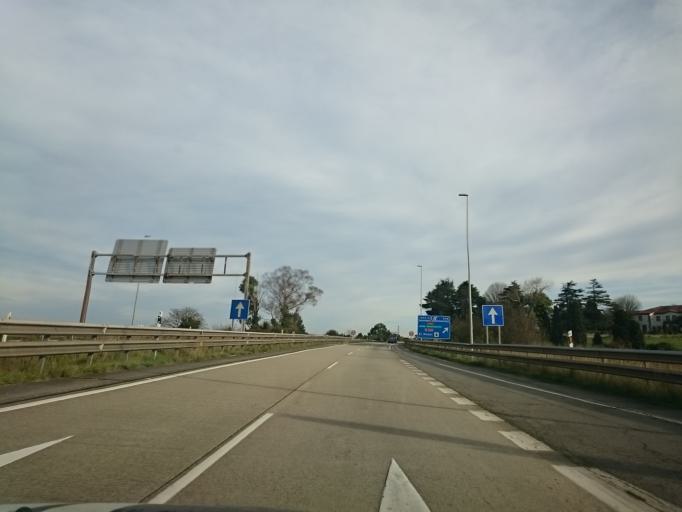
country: ES
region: Asturias
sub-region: Province of Asturias
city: Natahoyo
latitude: 43.5181
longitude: -5.7050
